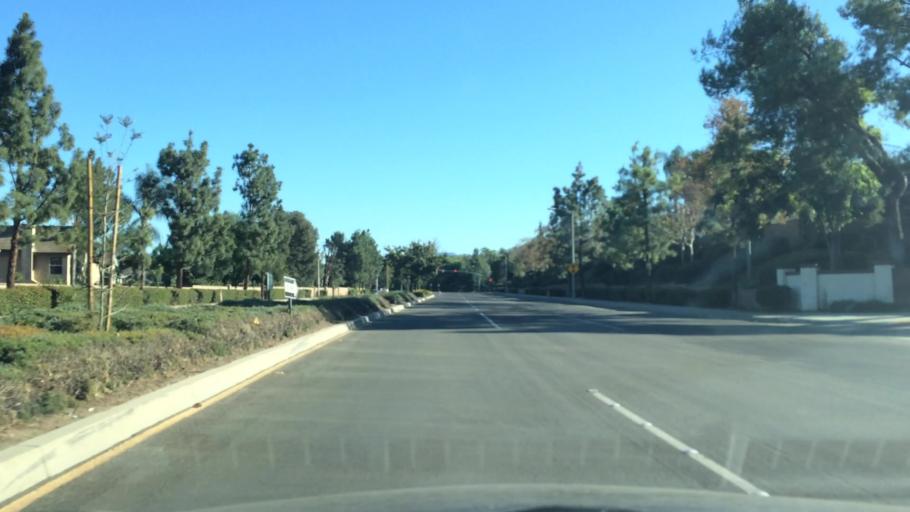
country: US
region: California
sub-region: San Bernardino County
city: Los Serranos
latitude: 33.9595
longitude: -117.6909
